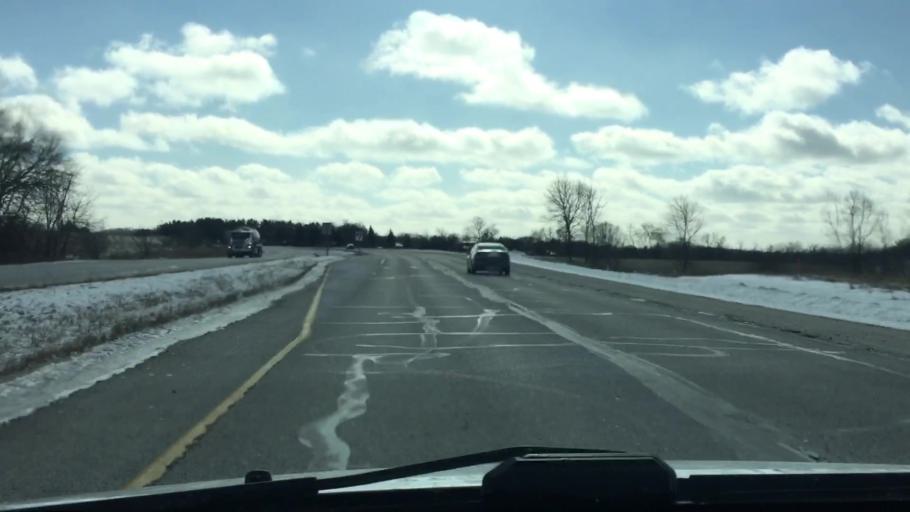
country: US
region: Wisconsin
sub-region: Waukesha County
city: Big Bend
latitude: 42.9271
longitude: -88.2289
